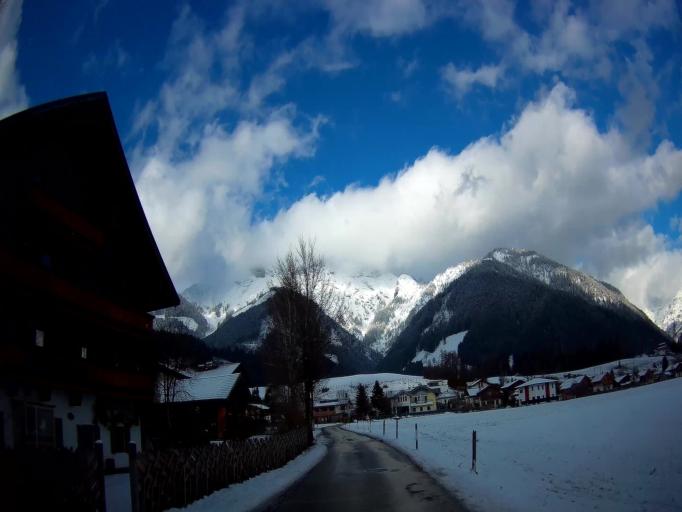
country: AT
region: Salzburg
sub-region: Politischer Bezirk Zell am See
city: Leogang
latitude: 47.4431
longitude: 12.7962
